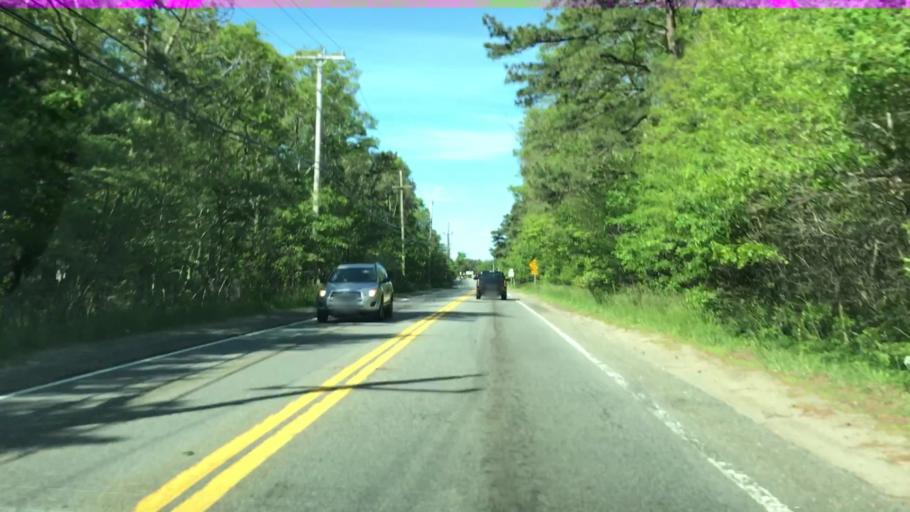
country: US
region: Massachusetts
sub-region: Barnstable County
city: Mashpee
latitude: 41.6206
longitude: -70.4833
